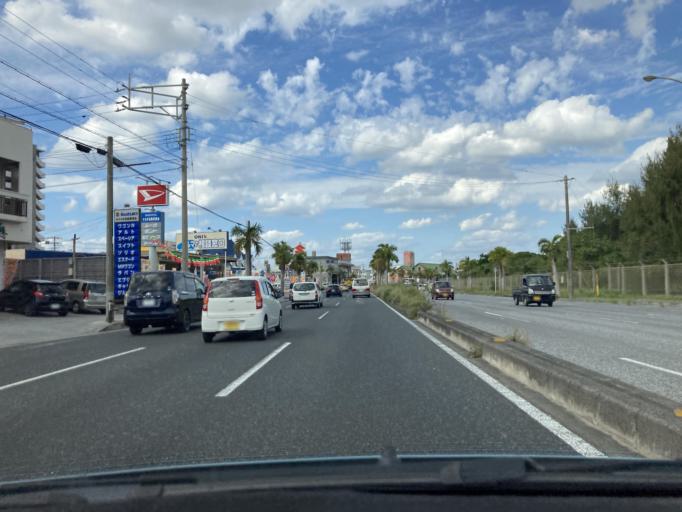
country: JP
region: Okinawa
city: Chatan
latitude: 26.3529
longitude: 127.7460
